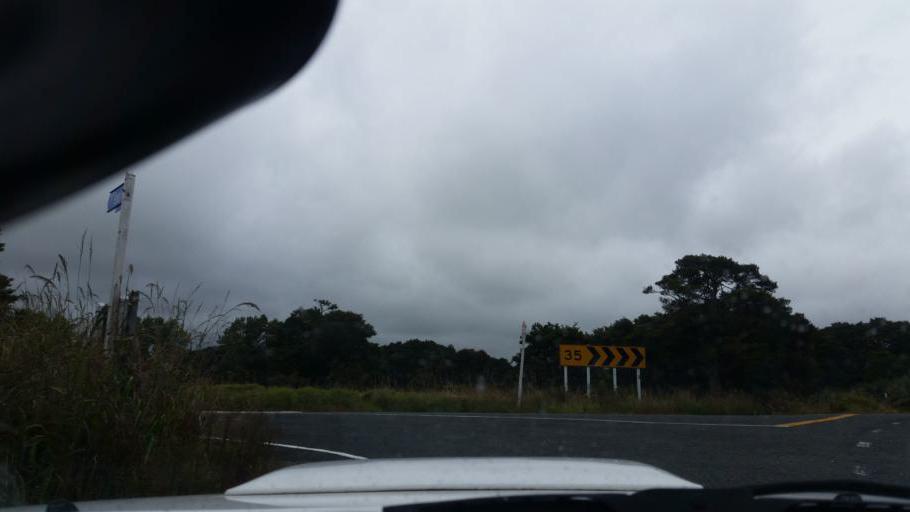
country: NZ
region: Auckland
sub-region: Auckland
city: Wellsford
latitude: -36.1386
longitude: 174.5074
